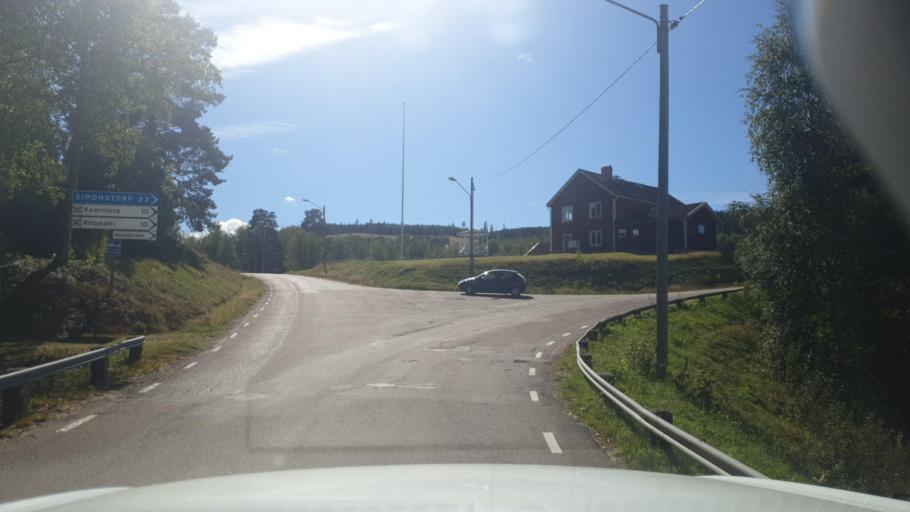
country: SE
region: Vaermland
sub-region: Torsby Kommun
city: Torsby
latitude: 60.1883
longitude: 12.6714
